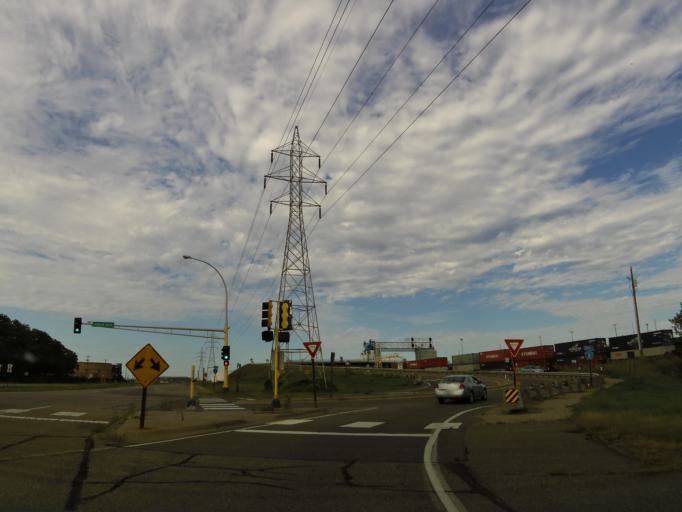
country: US
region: Minnesota
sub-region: Anoka County
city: Columbia Heights
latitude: 45.0427
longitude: -93.2747
